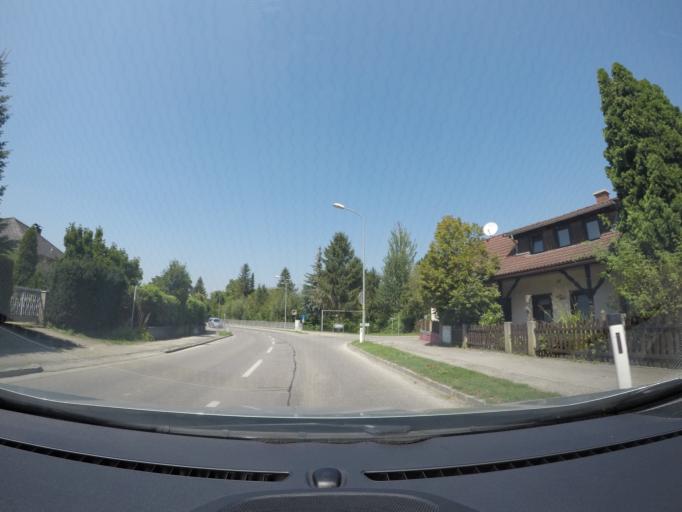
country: AT
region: Lower Austria
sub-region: Politischer Bezirk Sankt Polten
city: Eichgraben
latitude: 48.1840
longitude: 15.9652
